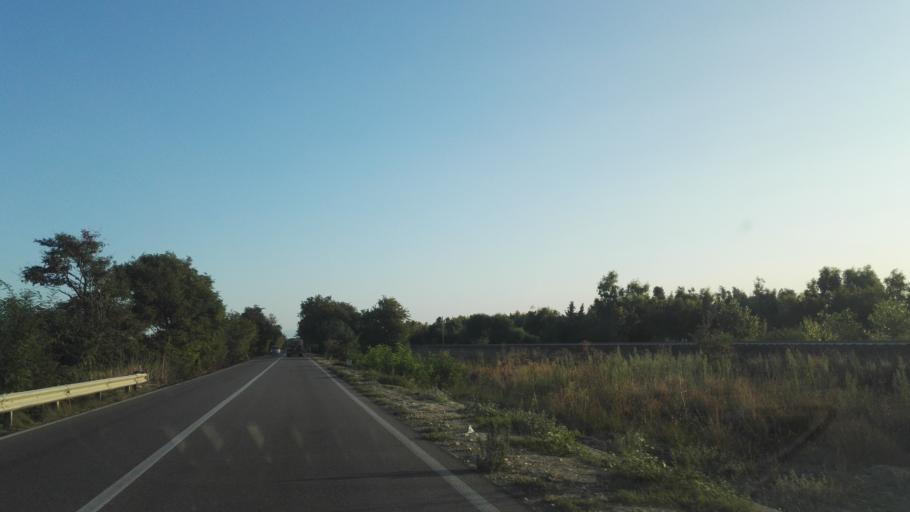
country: IT
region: Calabria
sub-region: Provincia di Catanzaro
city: Santa Caterina dello Ionio Marina
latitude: 38.5459
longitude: 16.5700
